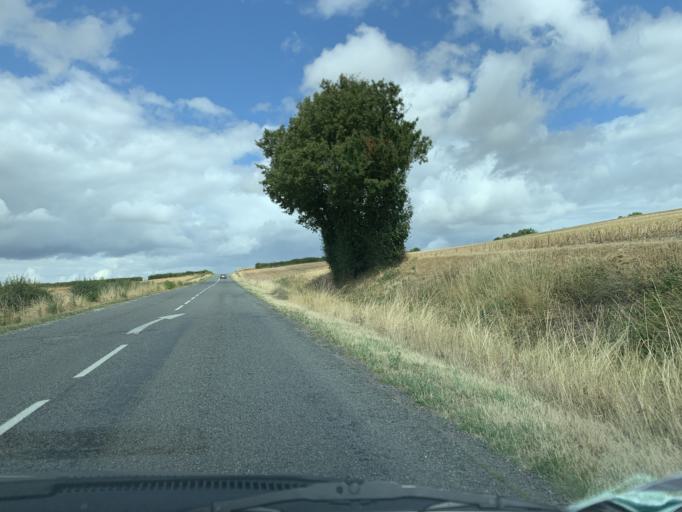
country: FR
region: Bourgogne
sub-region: Departement de la Nievre
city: Clamecy
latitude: 47.4069
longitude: 3.4519
